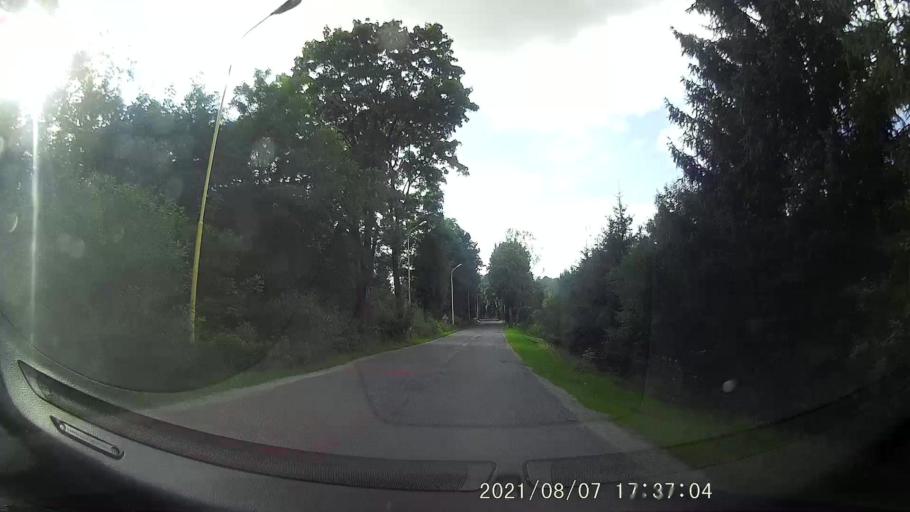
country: PL
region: Lower Silesian Voivodeship
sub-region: Powiat klodzki
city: Szczytna
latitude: 50.4021
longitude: 16.4580
